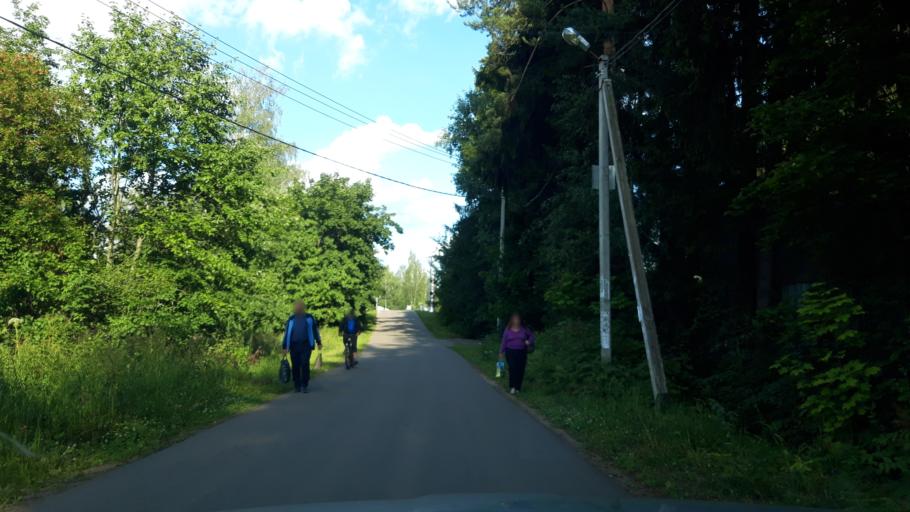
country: RU
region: Moskovskaya
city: Povarovo
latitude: 56.0623
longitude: 37.0823
